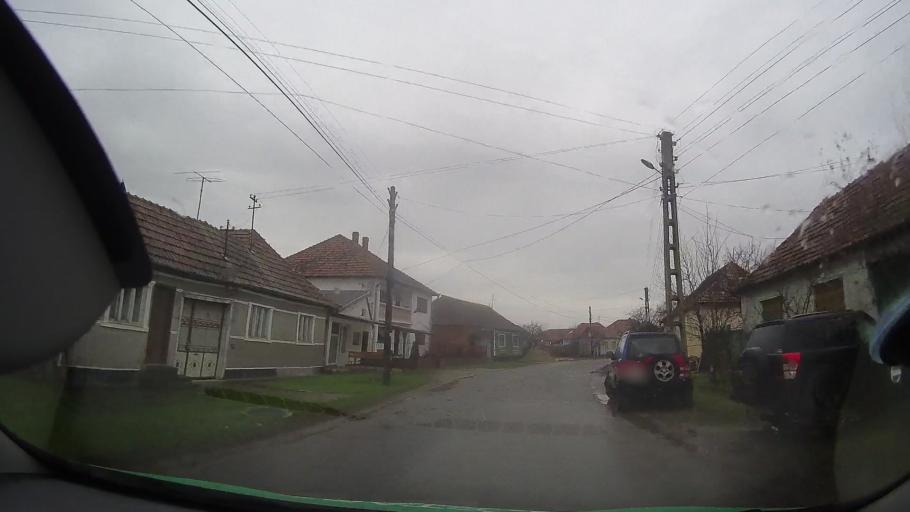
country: RO
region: Bihor
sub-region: Comuna Olcea
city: Olcea
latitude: 46.6832
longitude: 21.9693
